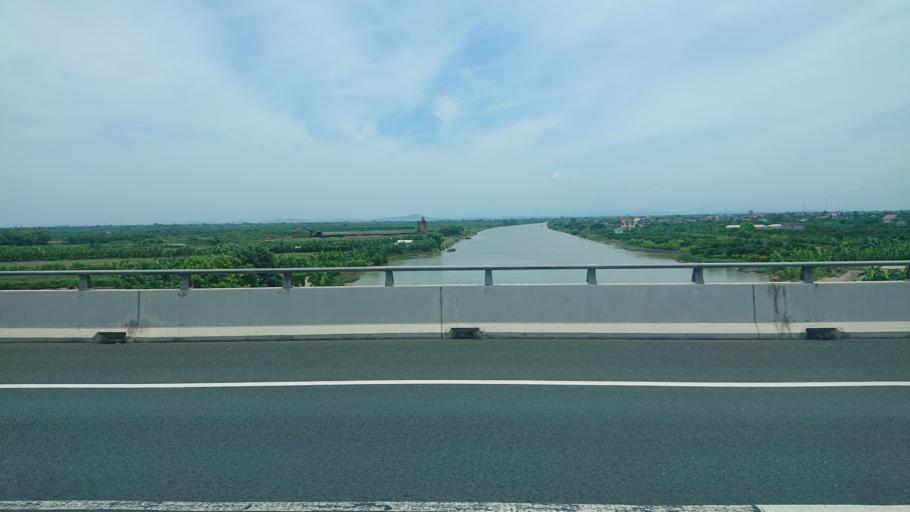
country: VN
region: Hai Duong
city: Tu Ky
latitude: 20.8329
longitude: 106.4424
